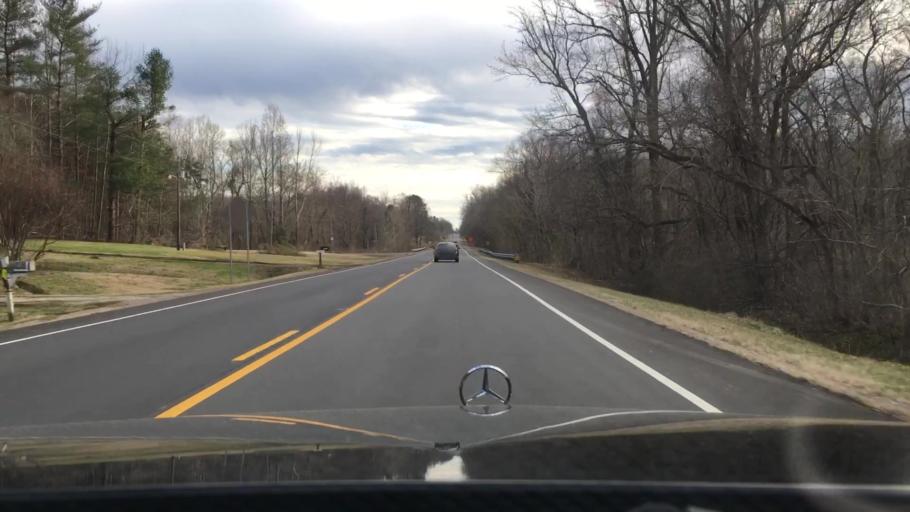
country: US
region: North Carolina
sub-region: Caswell County
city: Yanceyville
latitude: 36.4662
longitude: -79.3746
